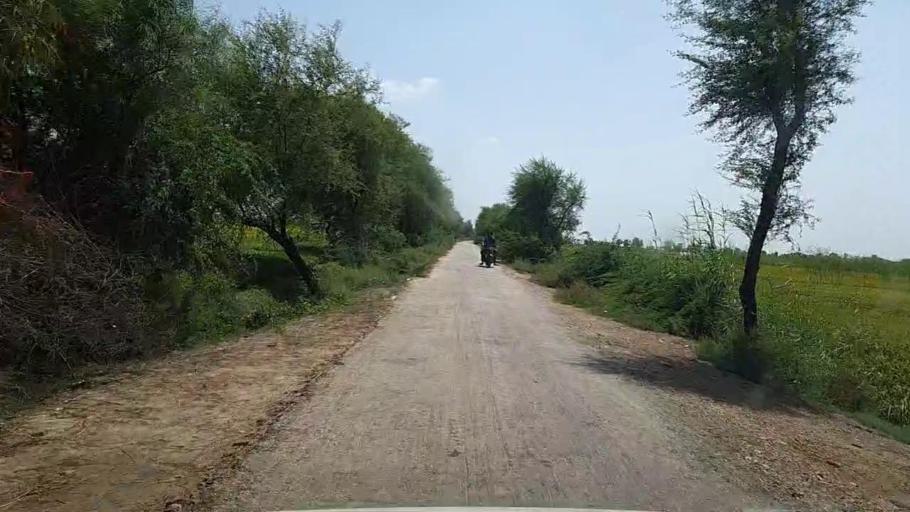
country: PK
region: Sindh
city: Kario
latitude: 24.6517
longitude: 68.5640
